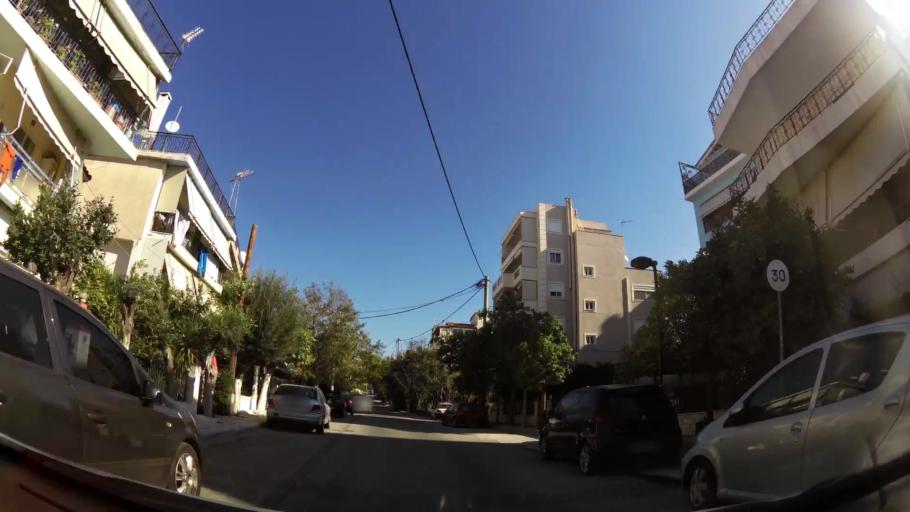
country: GR
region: Attica
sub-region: Nomarchia Athinas
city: Metamorfosi
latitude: 38.0639
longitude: 23.7688
